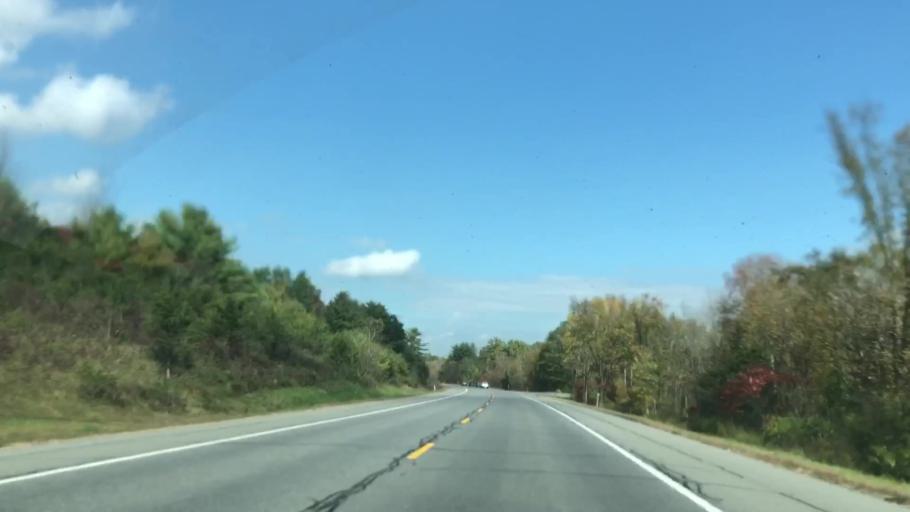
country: US
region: New York
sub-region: Washington County
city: Whitehall
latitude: 43.4447
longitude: -73.4525
